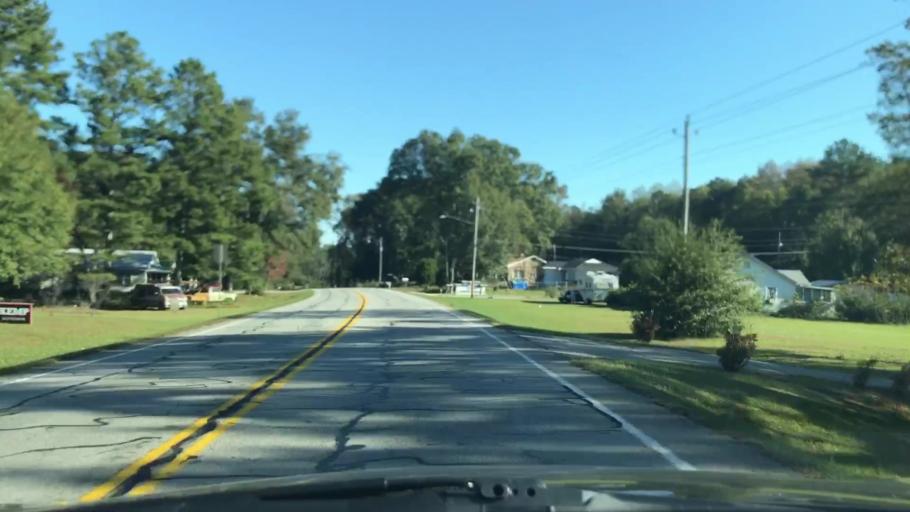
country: US
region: Georgia
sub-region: Carroll County
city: Villa Rica
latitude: 33.7528
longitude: -84.9040
